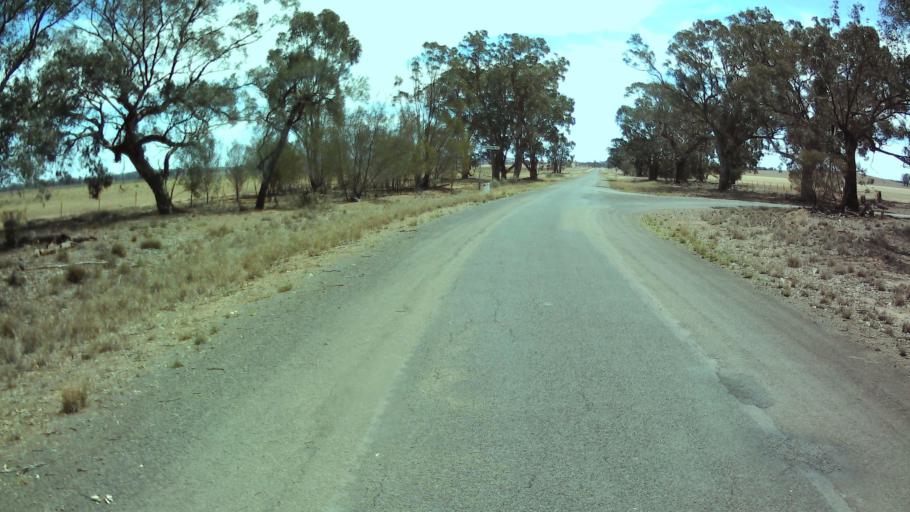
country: AU
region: New South Wales
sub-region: Weddin
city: Grenfell
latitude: -33.6417
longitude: 148.1897
